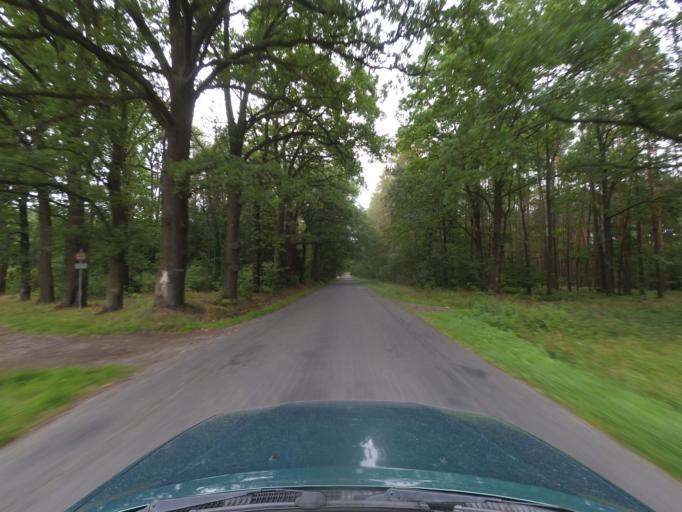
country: CZ
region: Plzensky
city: Holysov
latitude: 49.5517
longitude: 13.1406
